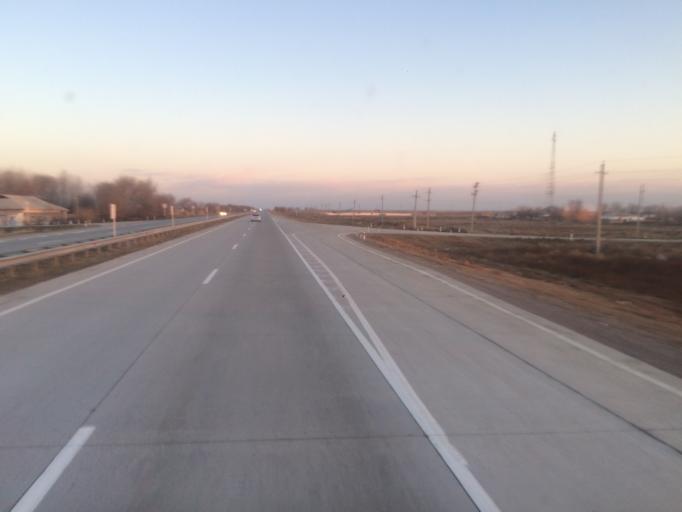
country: KZ
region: Ongtustik Qazaqstan
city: Bayaldyr
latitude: 43.0615
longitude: 68.6820
